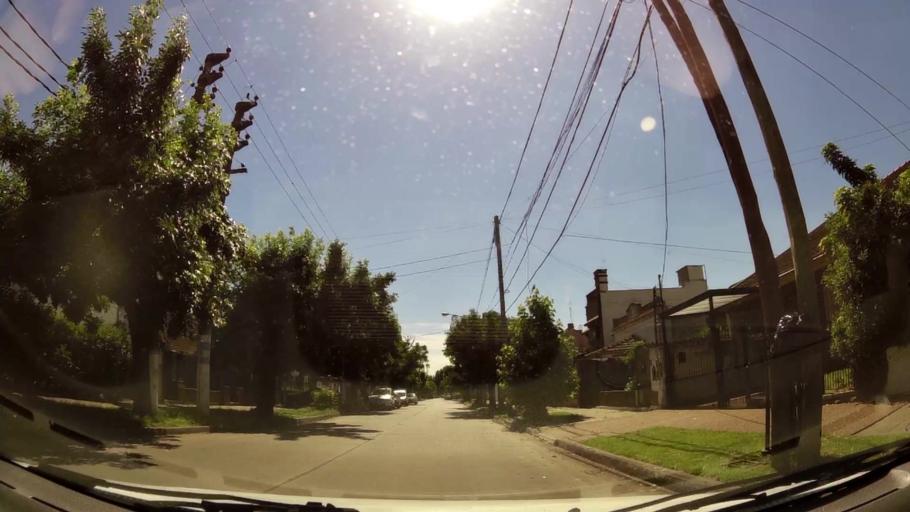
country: AR
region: Buenos Aires
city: Ituzaingo
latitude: -34.6621
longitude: -58.6639
